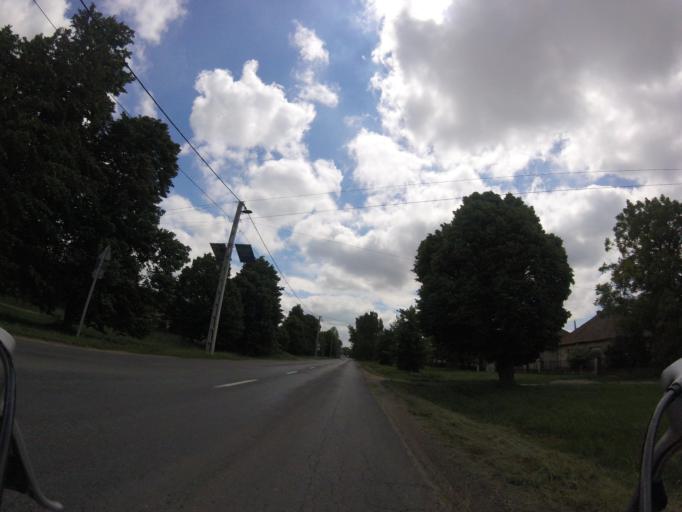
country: HU
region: Fejer
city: Sarosd
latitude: 47.0482
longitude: 18.6384
